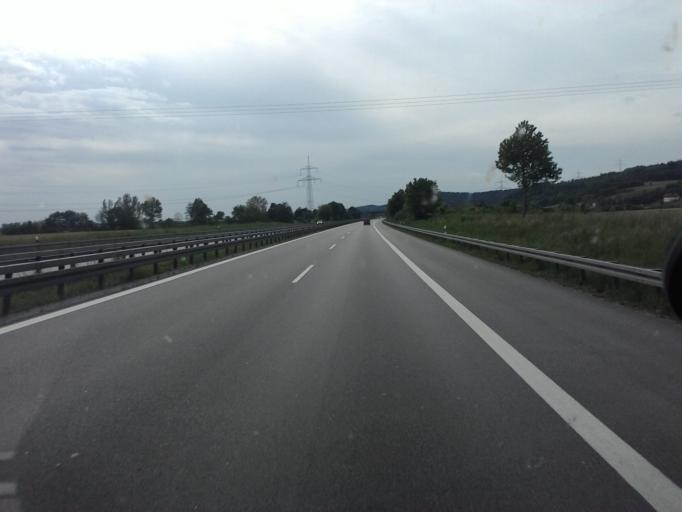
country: DE
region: Bavaria
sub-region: Lower Bavaria
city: Aholfing
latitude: 48.9779
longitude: 12.4737
